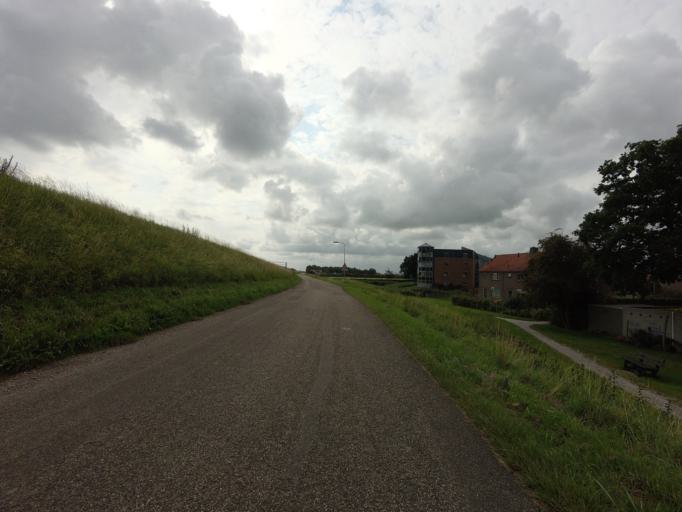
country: NL
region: North Holland
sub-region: Gemeente Hoorn
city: Hoorn
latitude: 52.6222
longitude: 5.0151
